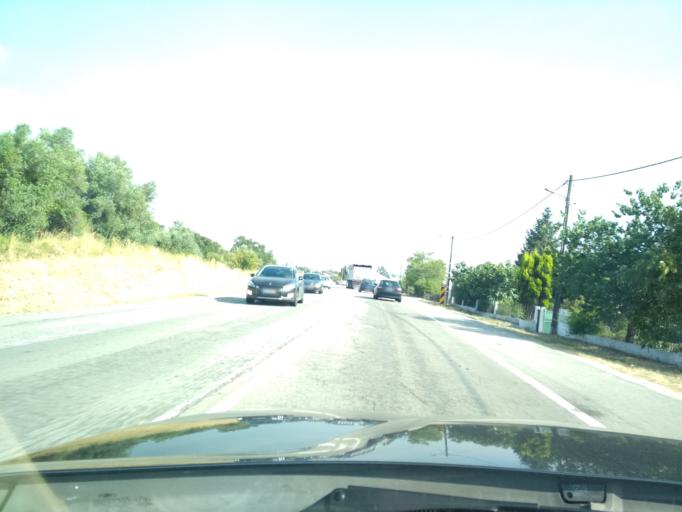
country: PT
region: Aveiro
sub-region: Mealhada
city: Mealhada
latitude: 40.3614
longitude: -8.4531
